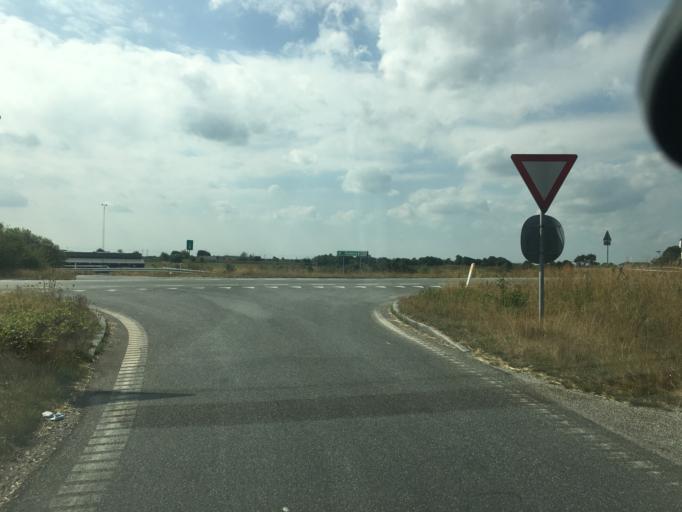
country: DK
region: South Denmark
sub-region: Aabenraa Kommune
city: Krusa
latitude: 54.9395
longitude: 9.3811
